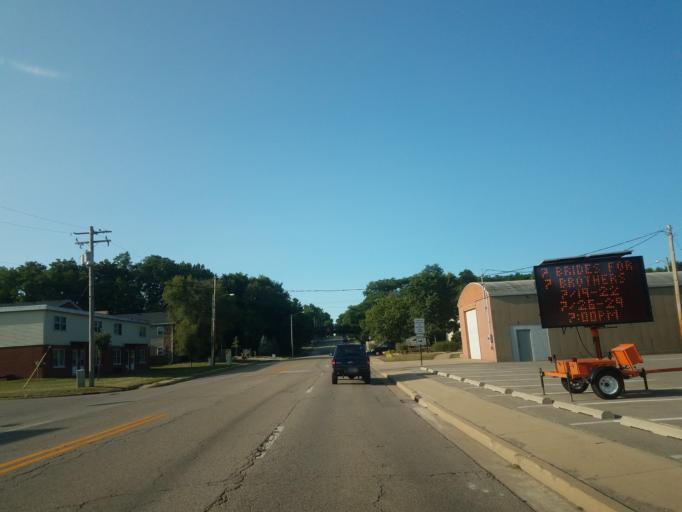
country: US
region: Illinois
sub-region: McLean County
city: Normal
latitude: 40.5036
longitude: -88.9823
